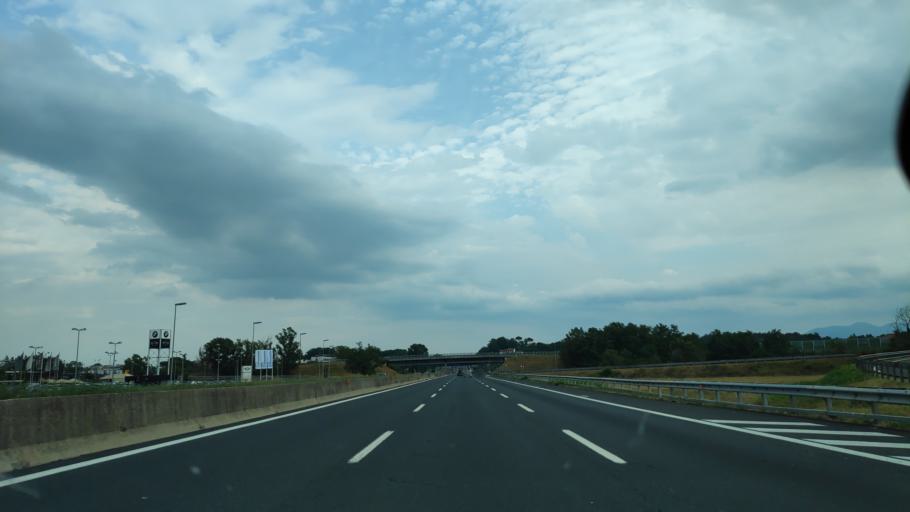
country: IT
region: Latium
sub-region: Provincia di Frosinone
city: Frosinone
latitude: 41.6207
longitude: 13.3091
